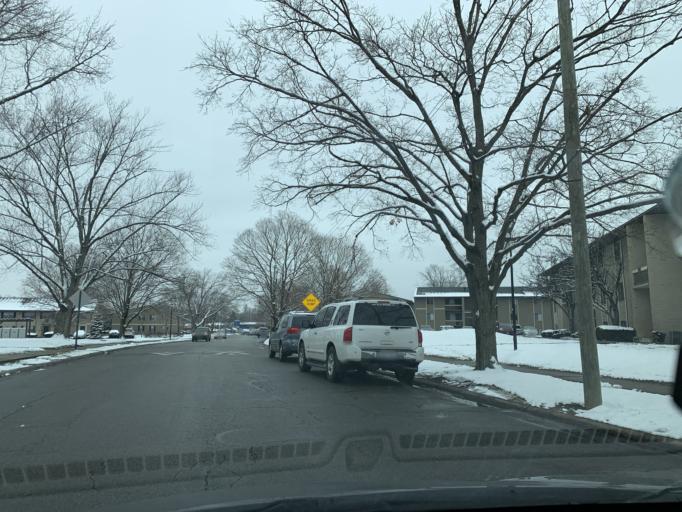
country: US
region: Ohio
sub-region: Franklin County
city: Minerva Park
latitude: 40.0548
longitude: -82.9727
